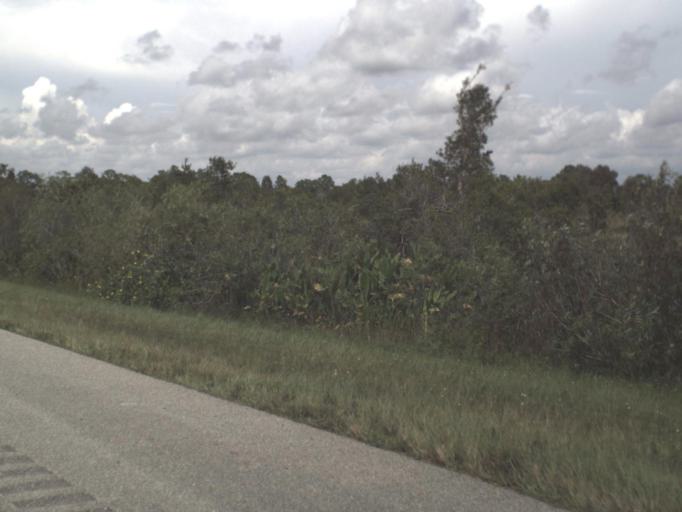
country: US
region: Florida
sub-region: Lee County
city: Suncoast Estates
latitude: 26.8033
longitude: -81.9209
